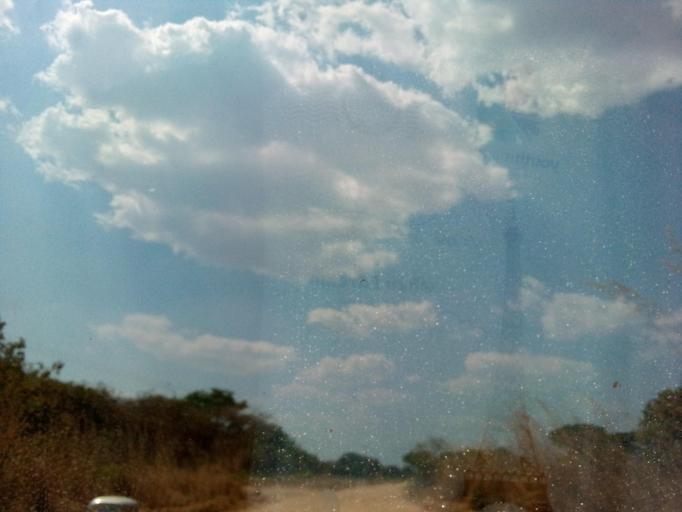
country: ZM
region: Northern
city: Mpika
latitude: -11.8426
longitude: 31.3855
